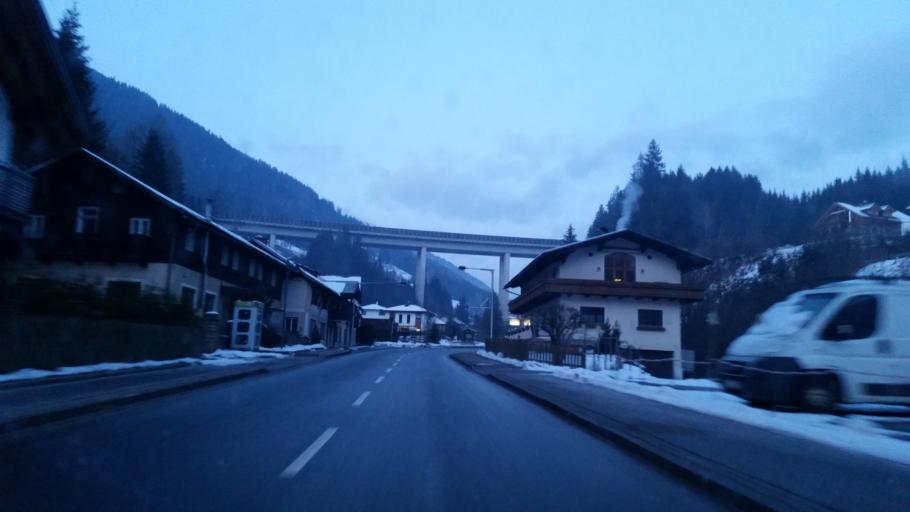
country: AT
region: Salzburg
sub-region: Politischer Bezirk Sankt Johann im Pongau
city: Huttau
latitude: 47.4227
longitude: 13.3457
